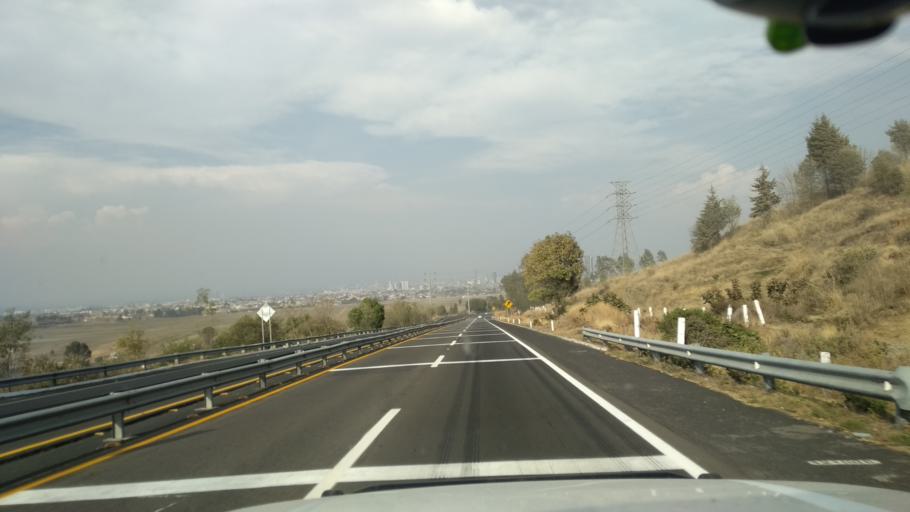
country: MX
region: Puebla
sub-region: Ocoyucan
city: Santa Martha Hidalgo
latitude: 18.9820
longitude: -98.3206
